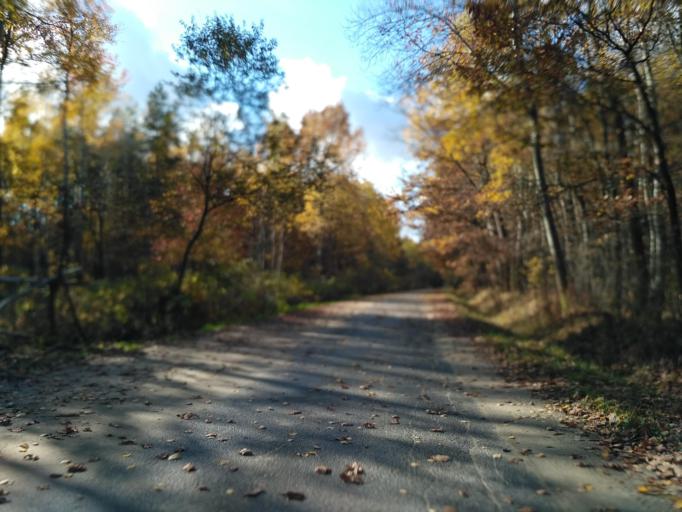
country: PL
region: Subcarpathian Voivodeship
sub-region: Powiat rzeszowski
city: Glogow Malopolski
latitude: 50.1377
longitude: 21.9348
